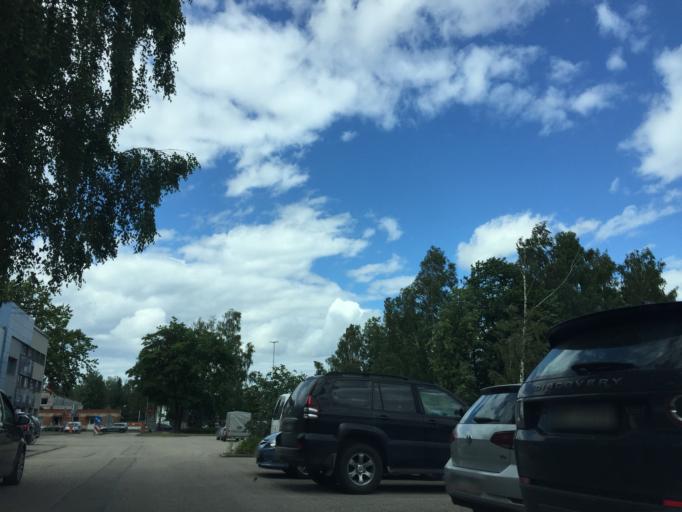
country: LV
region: Marupe
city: Marupe
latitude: 56.9438
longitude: 24.0332
